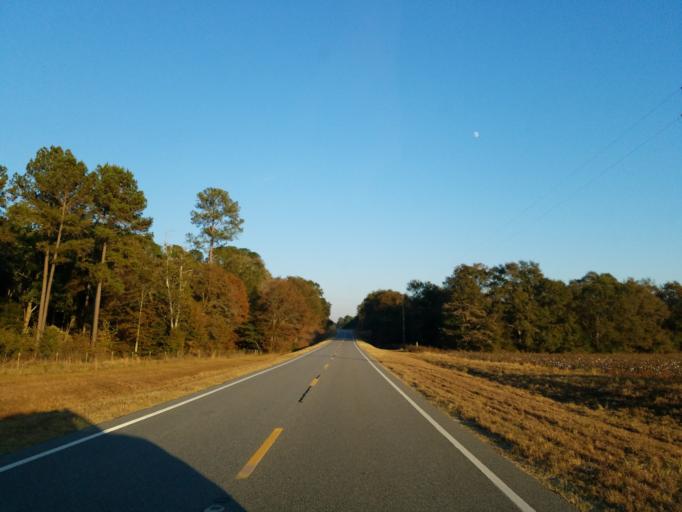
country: US
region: Georgia
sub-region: Turner County
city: Ashburn
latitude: 31.8240
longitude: -83.5595
